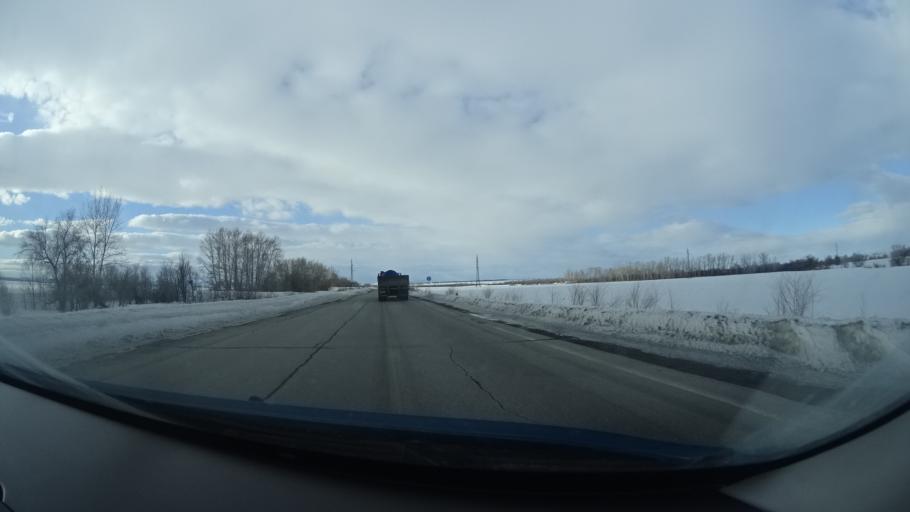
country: RU
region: Chelyabinsk
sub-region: Gorod Magnitogorsk
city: Magnitogorsk
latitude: 53.5828
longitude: 58.8849
